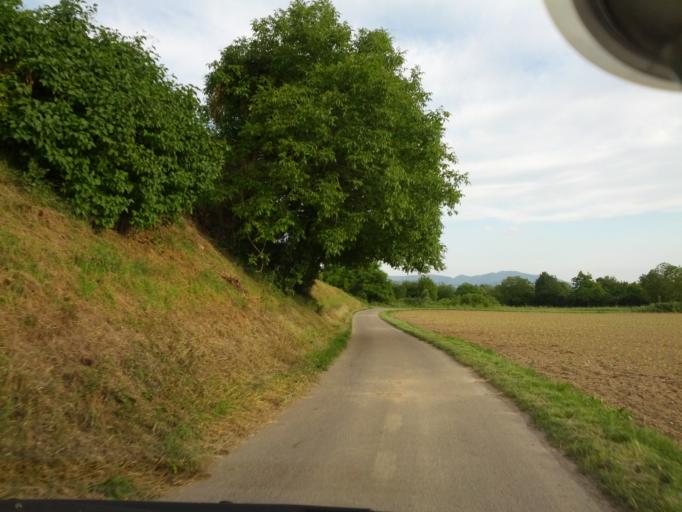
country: DE
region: Baden-Wuerttemberg
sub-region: Freiburg Region
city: Merdingen
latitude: 47.9714
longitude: 7.6765
